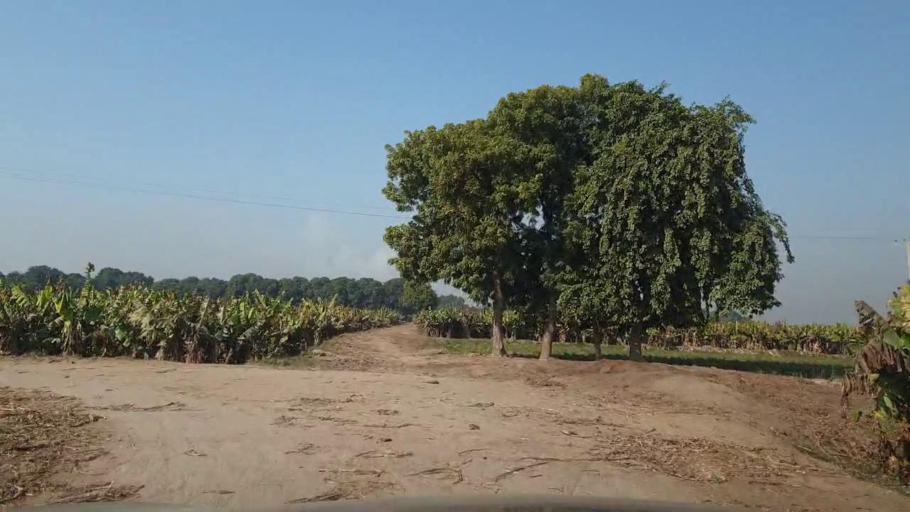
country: PK
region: Sindh
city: Tando Allahyar
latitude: 25.5268
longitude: 68.7203
